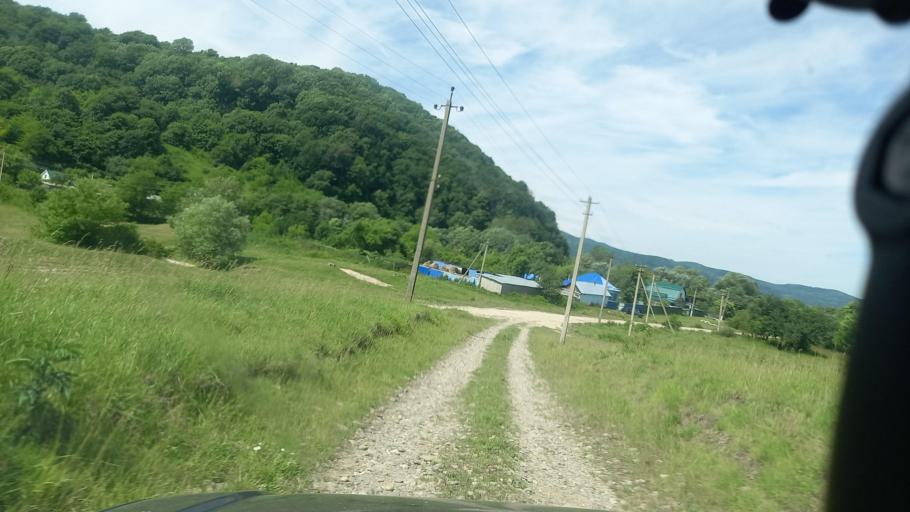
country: RU
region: Karachayevo-Cherkesiya
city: Kurdzhinovo
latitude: 44.1422
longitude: 41.0564
